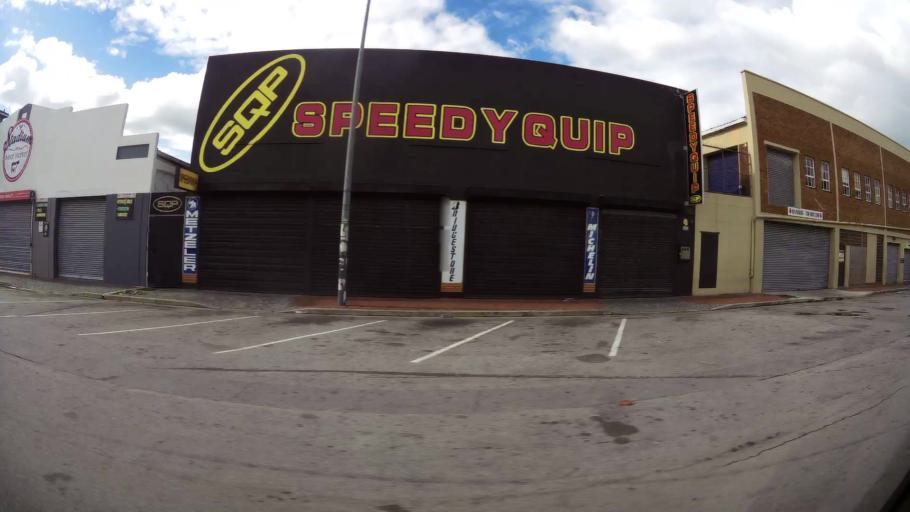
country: ZA
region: Eastern Cape
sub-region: Nelson Mandela Bay Metropolitan Municipality
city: Port Elizabeth
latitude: -33.9433
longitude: 25.6028
